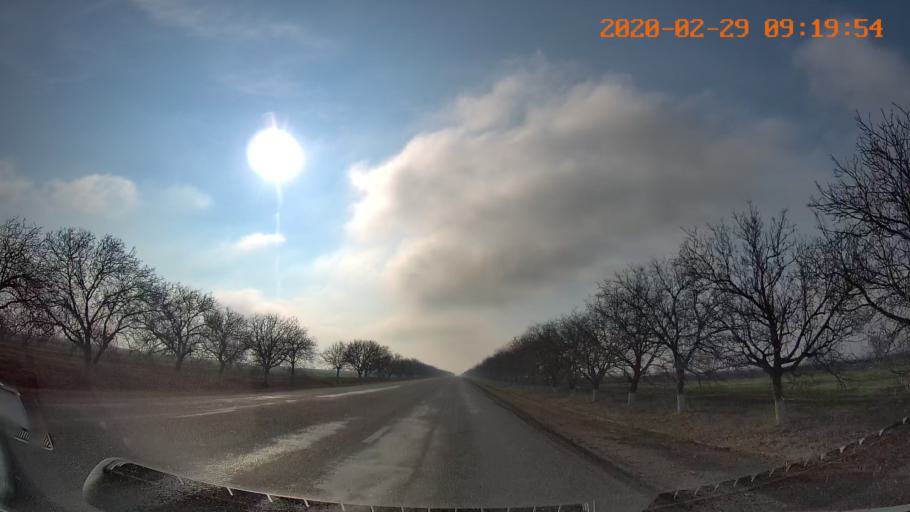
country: MD
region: Telenesti
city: Pervomaisc
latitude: 46.7564
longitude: 29.9435
